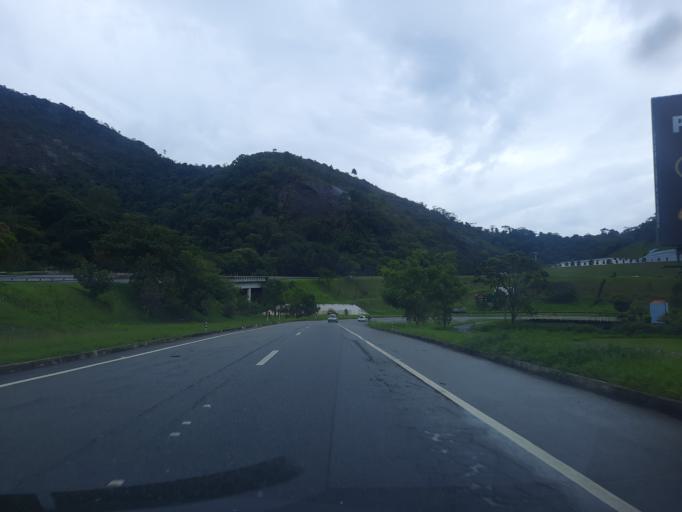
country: BR
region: Rio de Janeiro
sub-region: Petropolis
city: Petropolis
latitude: -22.4100
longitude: -43.1491
